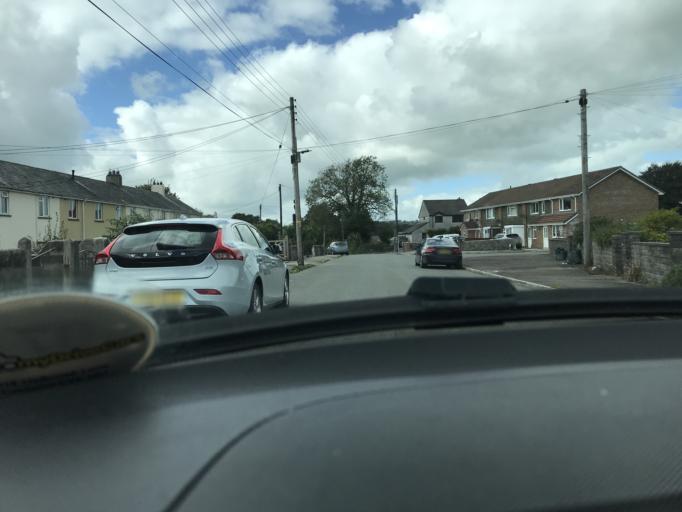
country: GB
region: England
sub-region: Devon
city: Tavistock
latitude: 50.5483
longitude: -4.1321
